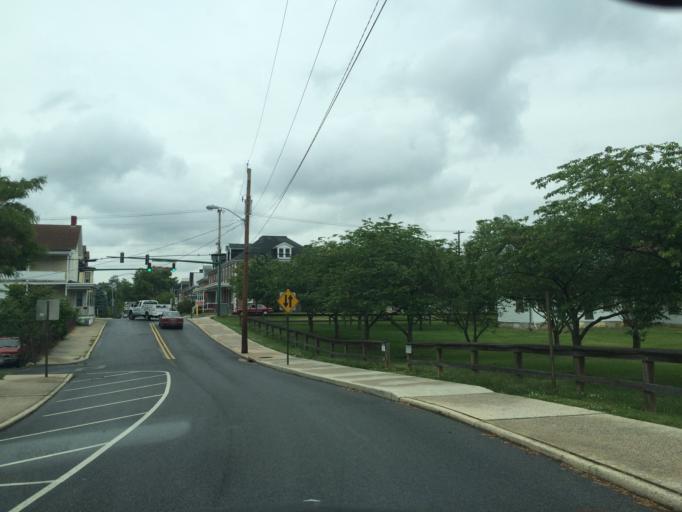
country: US
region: Maryland
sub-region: Washington County
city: Hagerstown
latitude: 39.6448
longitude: -77.7115
